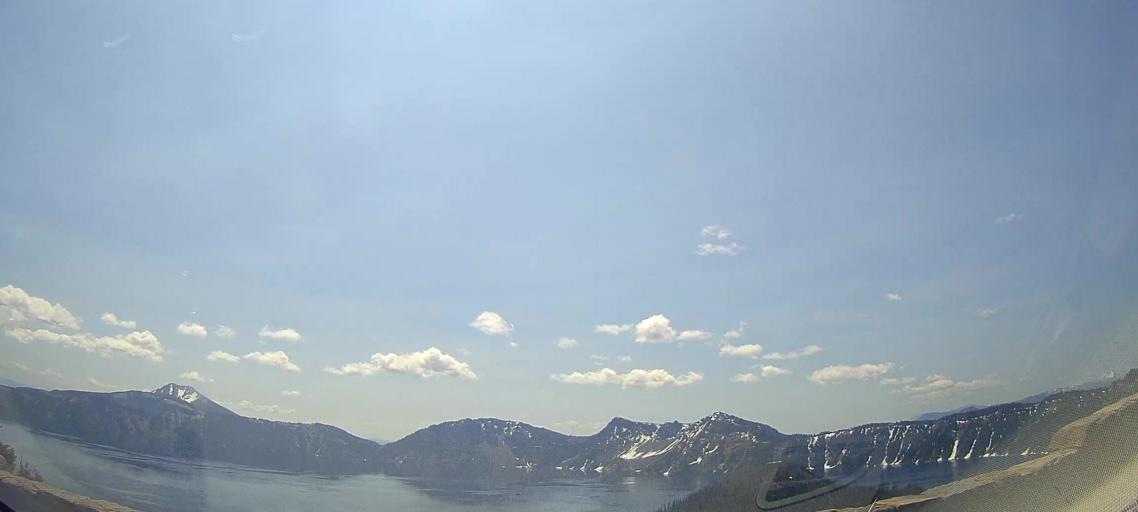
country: US
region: Oregon
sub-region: Jackson County
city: Shady Cove
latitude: 42.9619
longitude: -122.1568
